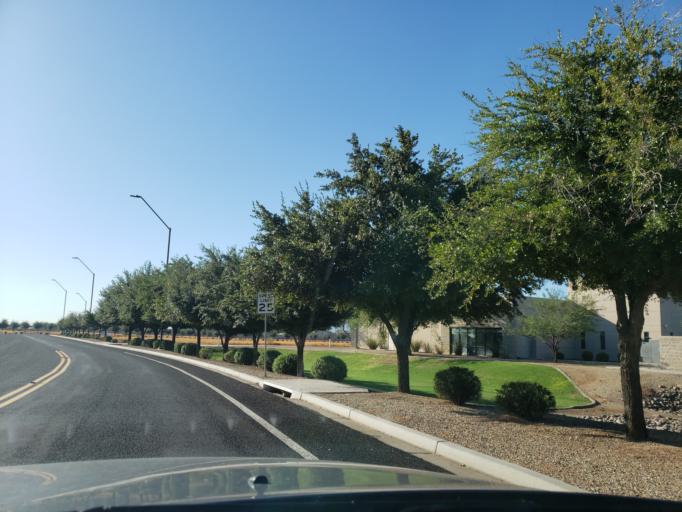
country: US
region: Arizona
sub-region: Maricopa County
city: Tolleson
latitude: 33.4459
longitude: -112.3024
